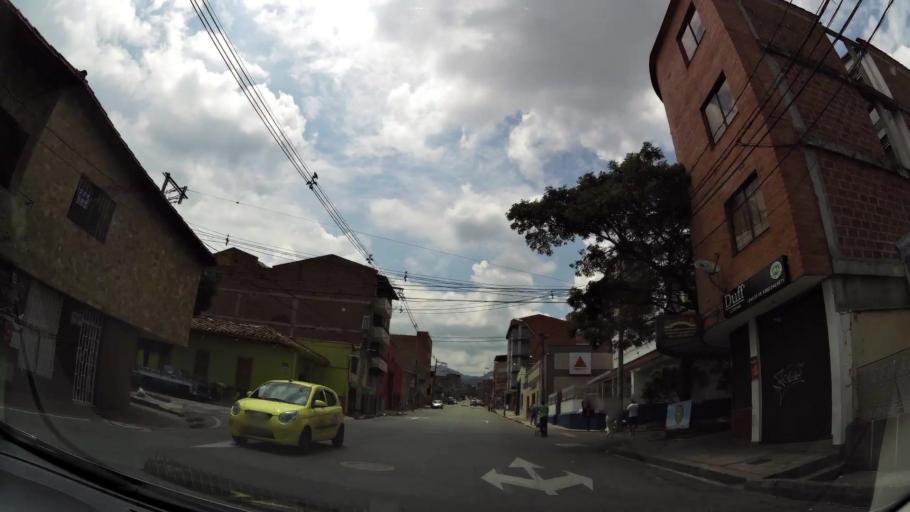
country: CO
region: Antioquia
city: Medellin
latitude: 6.2495
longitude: -75.6077
